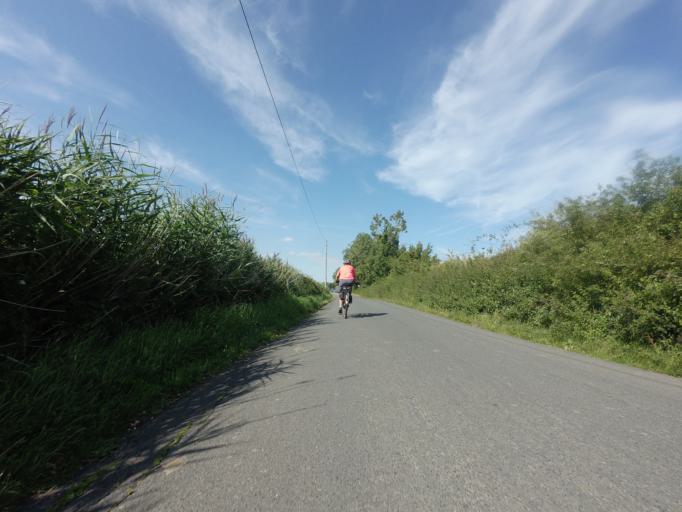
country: GB
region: England
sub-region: Kent
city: Tenterden
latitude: 50.9998
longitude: 0.6848
